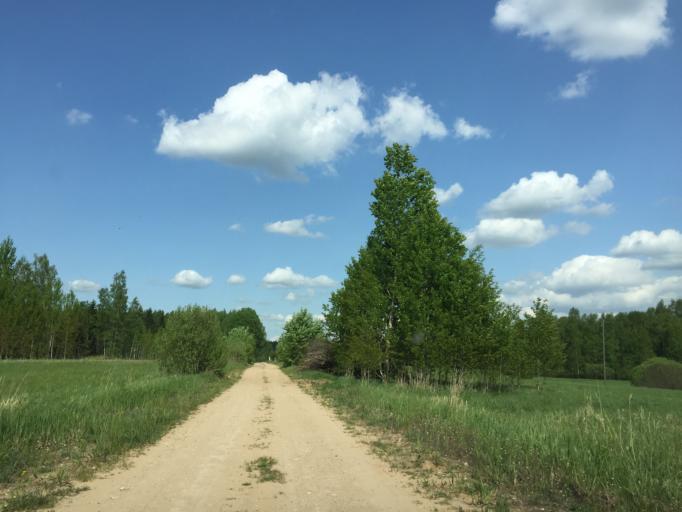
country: LV
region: Baldone
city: Baldone
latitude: 56.7898
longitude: 24.4163
